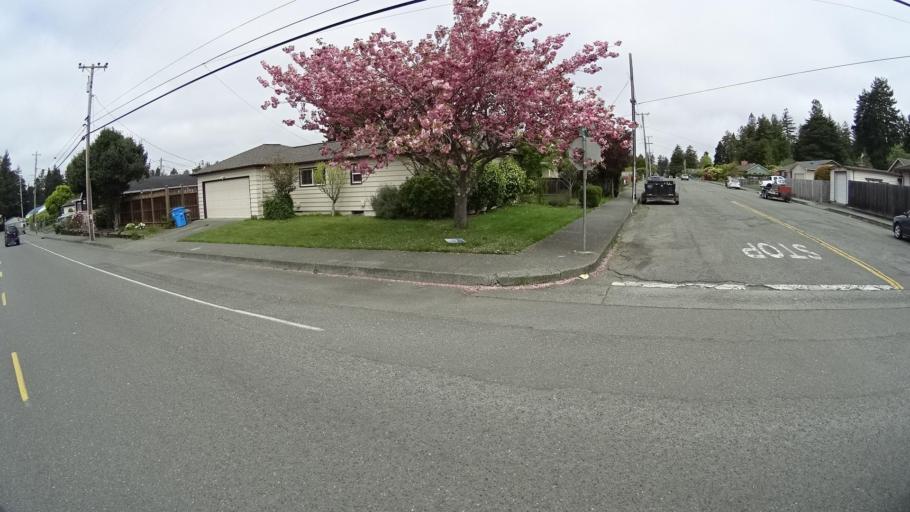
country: US
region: California
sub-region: Humboldt County
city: Cutten
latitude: 40.7659
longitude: -124.1415
